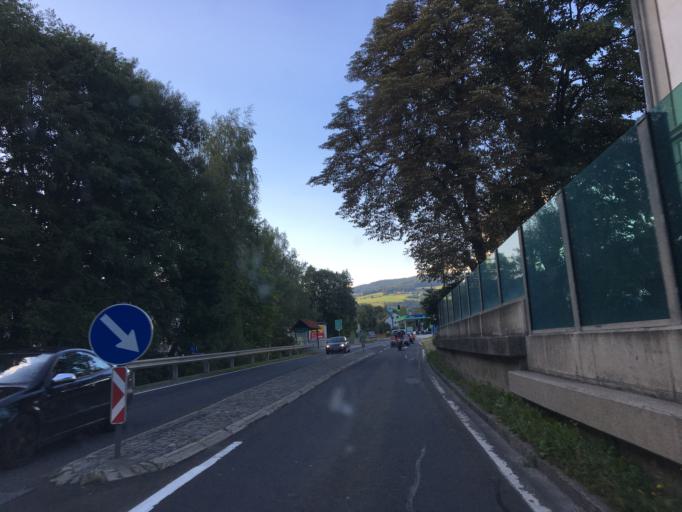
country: AT
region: Styria
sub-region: Politischer Bezirk Murau
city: Sankt Marein bei Neumarkt
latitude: 47.0659
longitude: 14.4305
